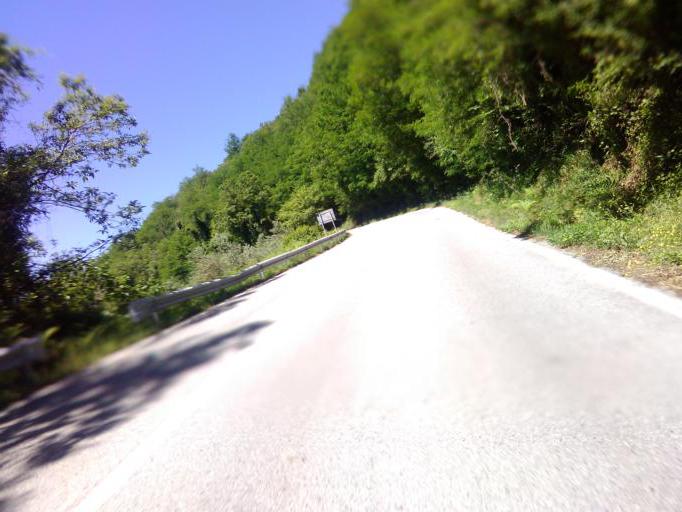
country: IT
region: Tuscany
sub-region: Provincia di Massa-Carrara
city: Pontremoli
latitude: 44.4008
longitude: 9.8871
